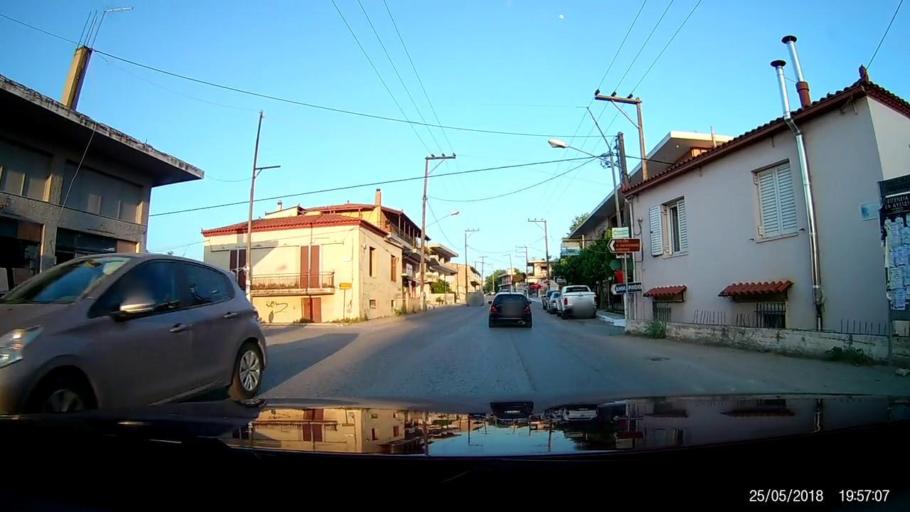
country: GR
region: Central Greece
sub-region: Nomos Evvoias
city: Vasilikon
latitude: 38.4272
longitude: 23.6654
